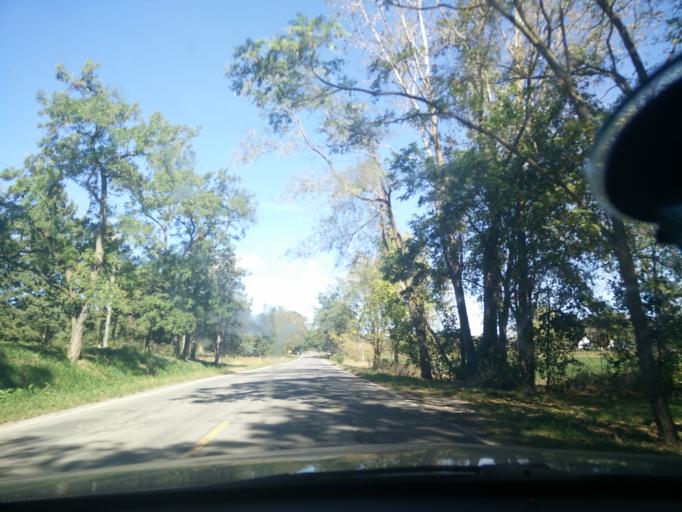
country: US
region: Michigan
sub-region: Oakland County
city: South Lyon
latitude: 42.4248
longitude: -83.5898
